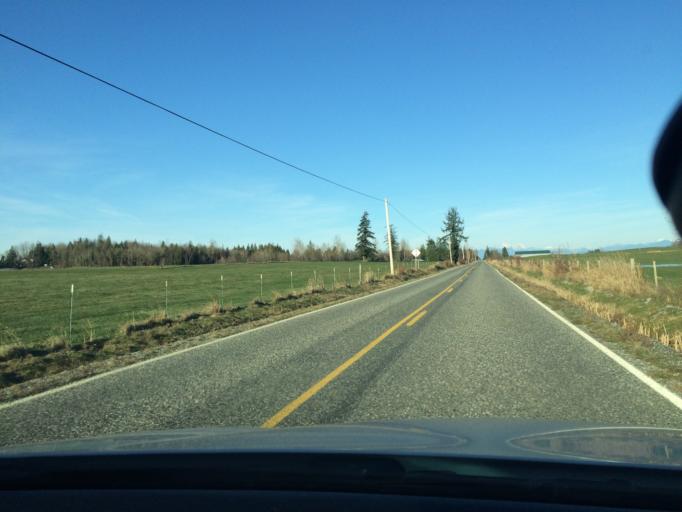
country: US
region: Washington
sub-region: Whatcom County
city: Everson
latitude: 48.8626
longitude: -122.3981
